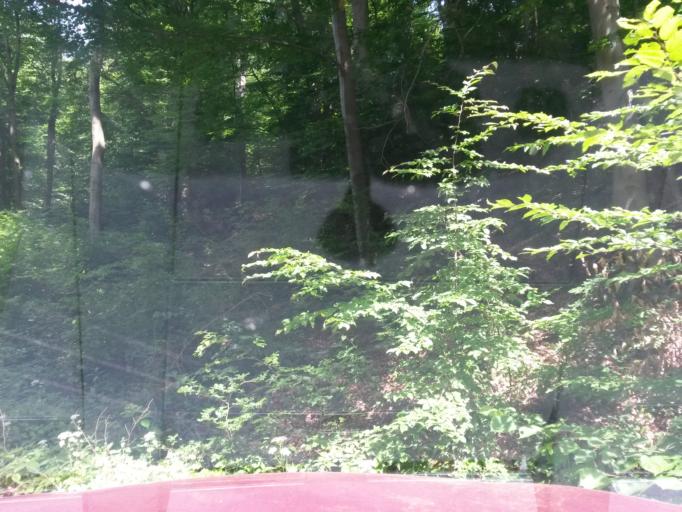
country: SK
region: Kosicky
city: Kosice
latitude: 48.7387
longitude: 21.1132
